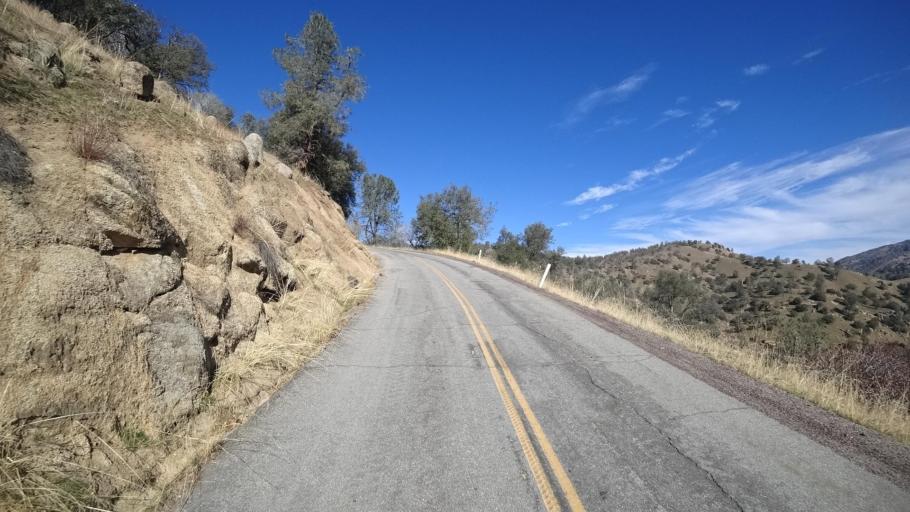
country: US
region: California
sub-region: Kern County
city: Alta Sierra
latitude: 35.6318
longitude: -118.7580
